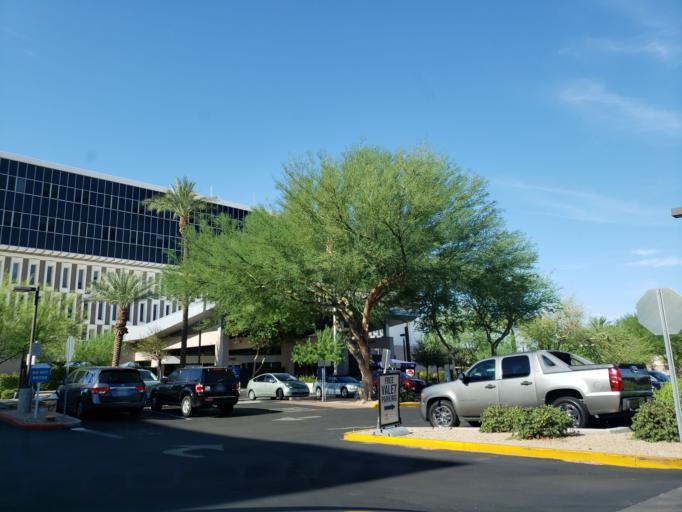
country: US
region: Arizona
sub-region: Maricopa County
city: Glendale
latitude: 33.5706
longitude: -112.0705
